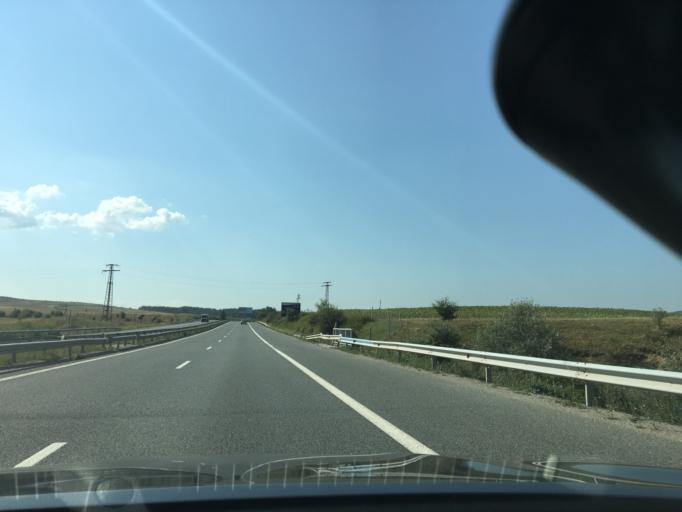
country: BG
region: Pernik
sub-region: Obshtina Pernik
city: Pernik
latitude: 42.5835
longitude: 23.1209
